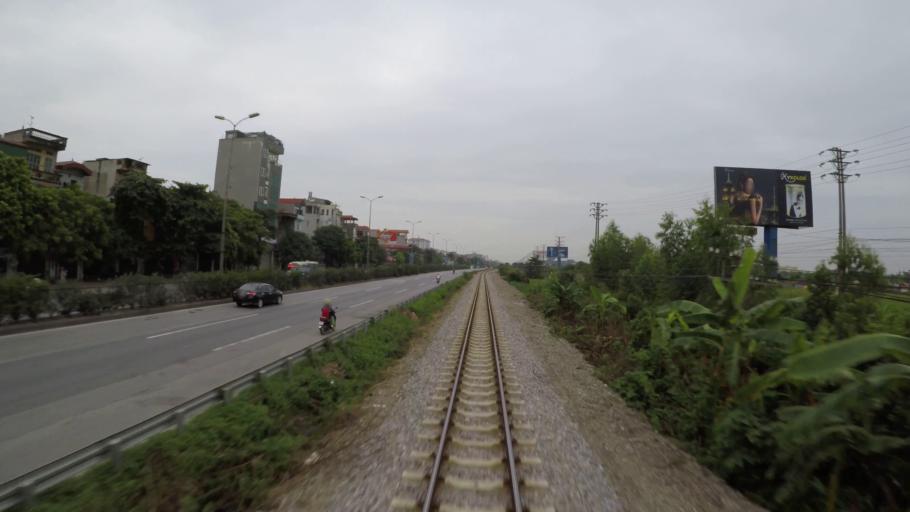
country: VN
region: Hung Yen
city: Nhu Quynh
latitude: 20.9867
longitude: 105.9771
